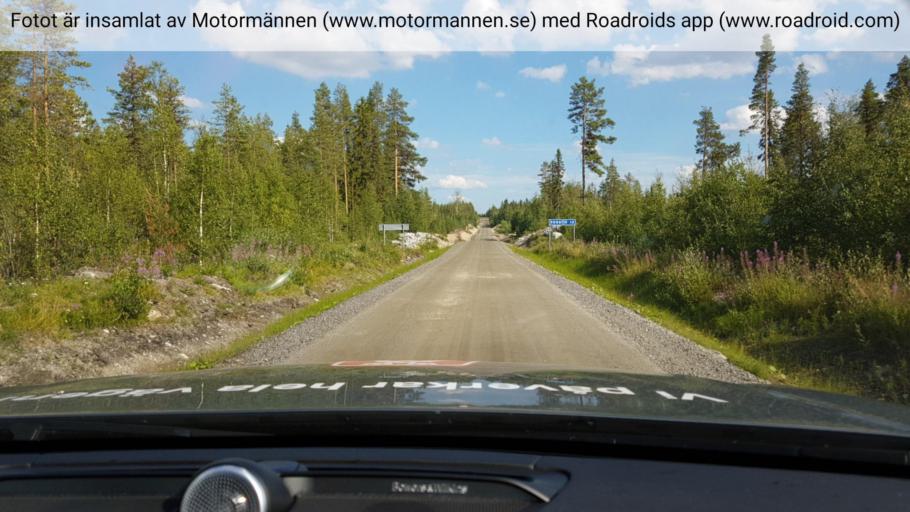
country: SE
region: Vaesterbotten
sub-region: Dorotea Kommun
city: Dorotea
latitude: 63.9328
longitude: 16.1052
